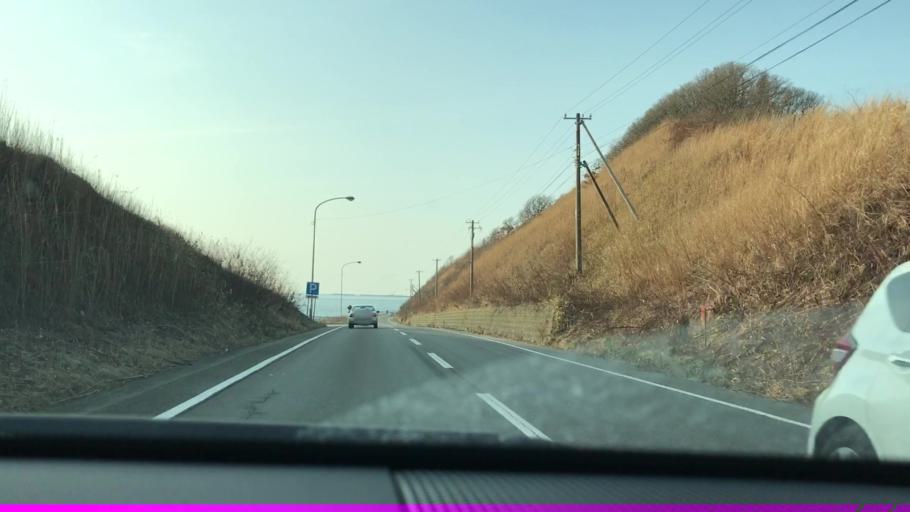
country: JP
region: Hokkaido
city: Shizunai-furukawacho
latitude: 42.2324
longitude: 142.6066
